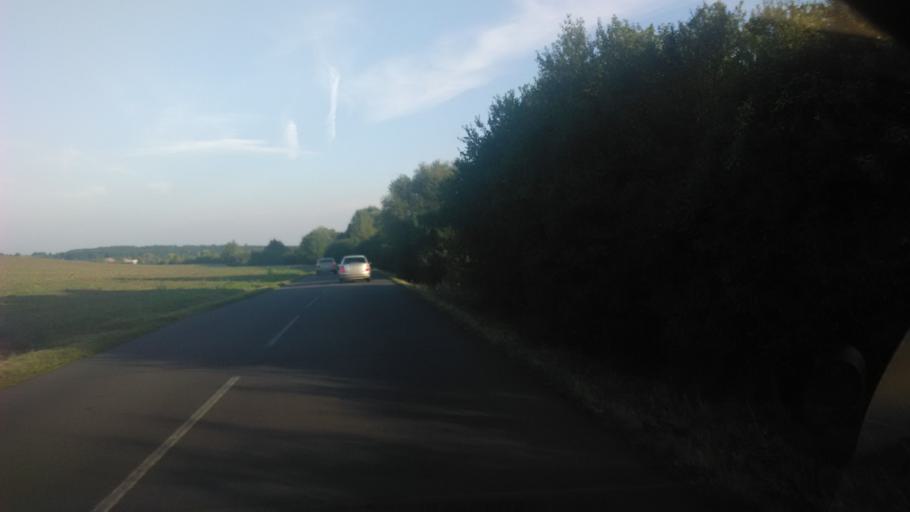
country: SK
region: Banskobystricky
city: Dudince
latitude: 48.1923
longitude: 18.8289
